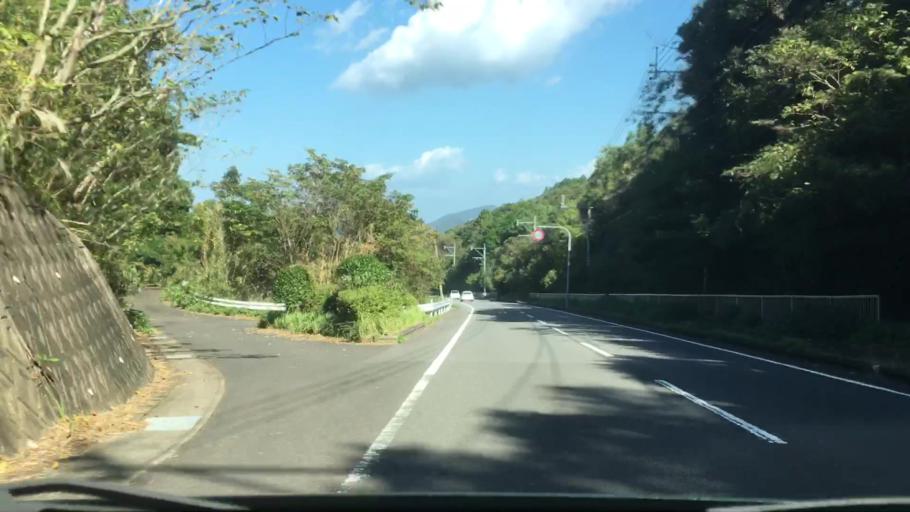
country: JP
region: Nagasaki
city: Sasebo
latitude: 32.9799
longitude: 129.6461
